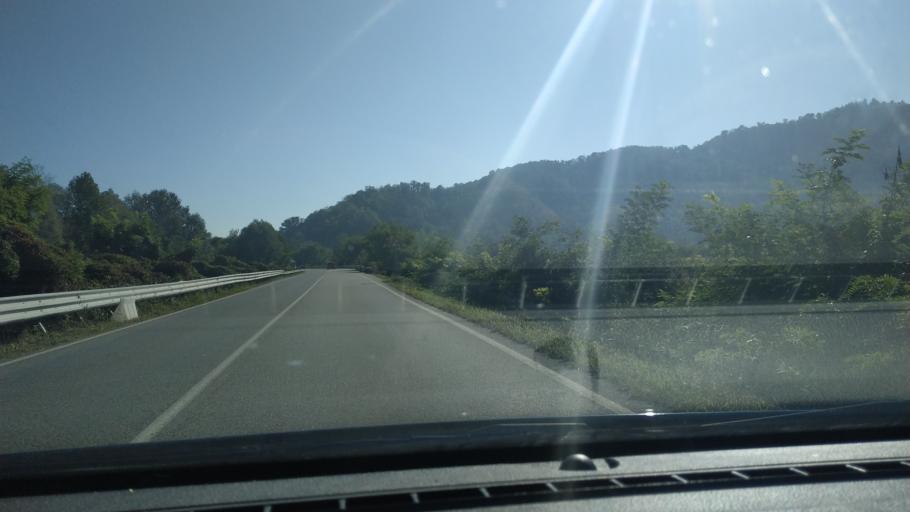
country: IT
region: Piedmont
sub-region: Provincia di Torino
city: San Sebastiano da Po
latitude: 45.1675
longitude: 7.9661
